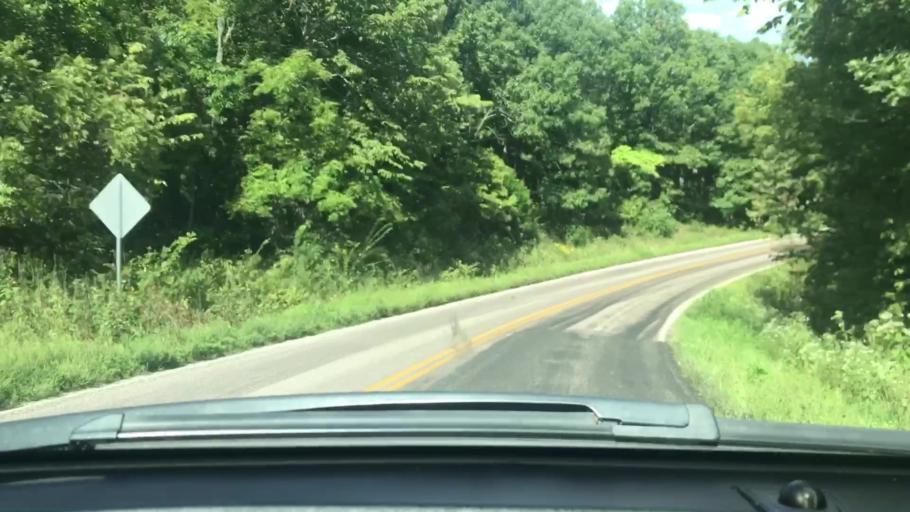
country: US
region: Missouri
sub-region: Wright County
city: Hartville
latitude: 37.3785
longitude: -92.3700
